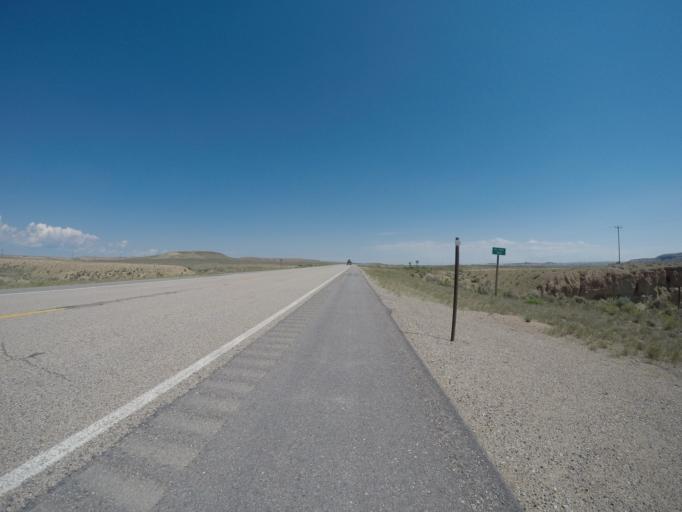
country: US
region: Wyoming
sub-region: Sublette County
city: Marbleton
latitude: 42.4243
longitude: -110.1107
